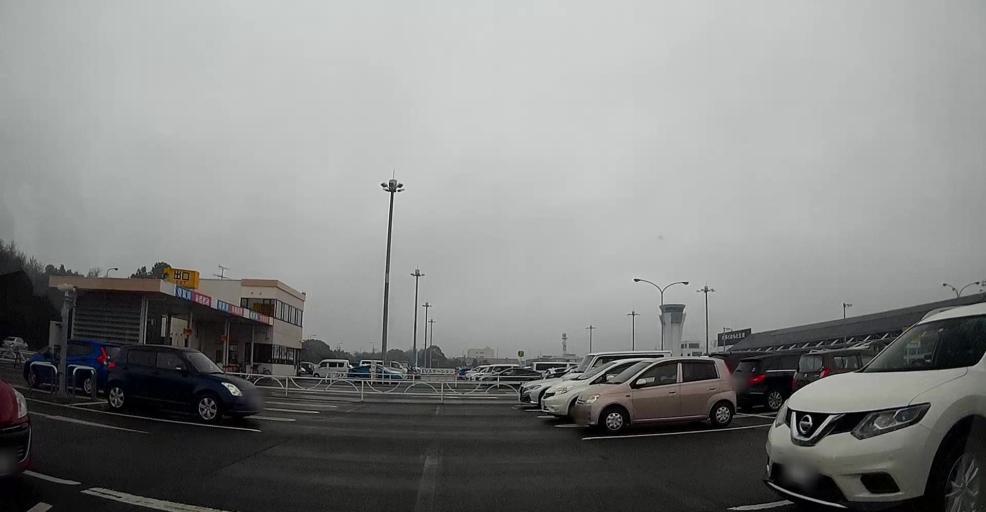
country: JP
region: Kumamoto
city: Ozu
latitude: 32.8339
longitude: 130.8600
